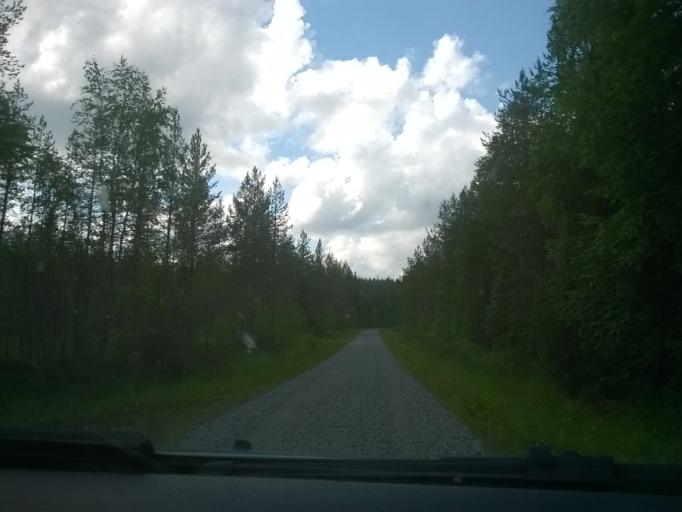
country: FI
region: Kainuu
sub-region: Kehys-Kainuu
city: Kuhmo
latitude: 64.4505
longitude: 29.6930
